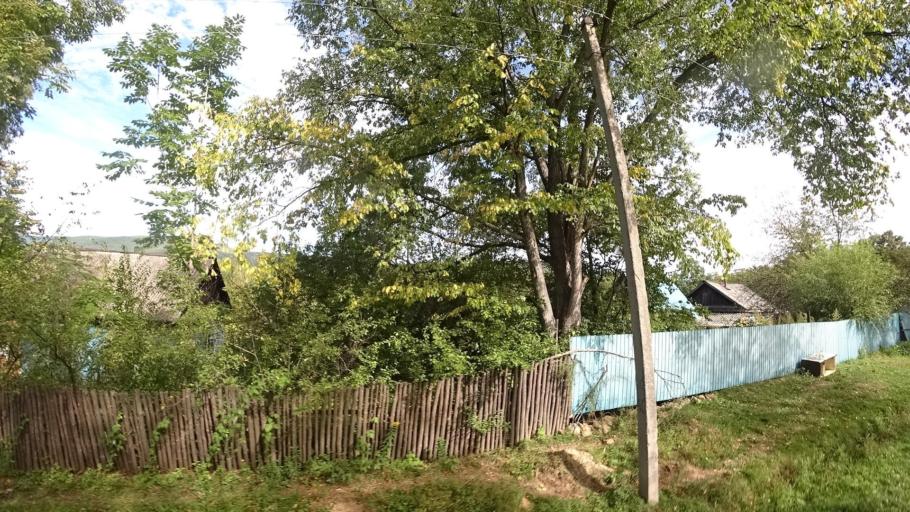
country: RU
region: Primorskiy
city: Yakovlevka
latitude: 44.3889
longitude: 133.6068
